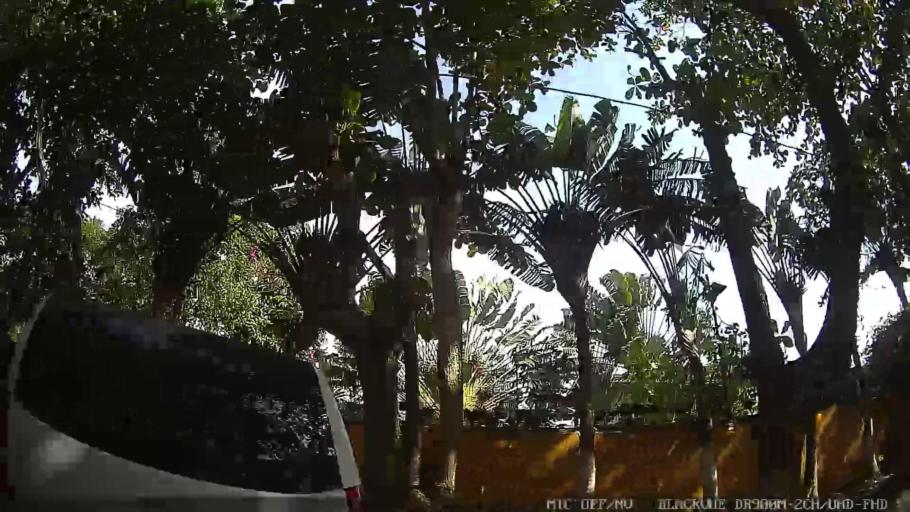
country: BR
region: Sao Paulo
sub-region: Guaruja
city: Guaruja
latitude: -23.9804
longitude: -46.1992
